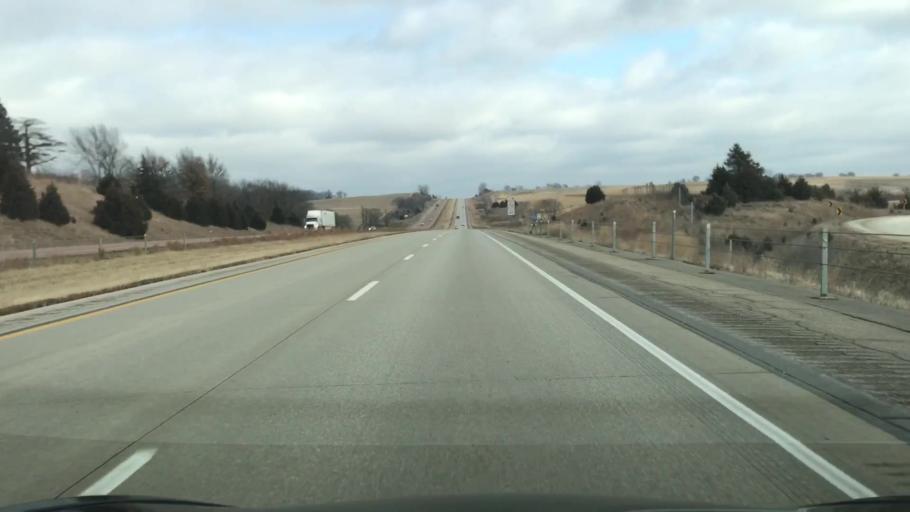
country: US
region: Iowa
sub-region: Guthrie County
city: Guthrie Center
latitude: 41.4960
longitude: -94.5108
